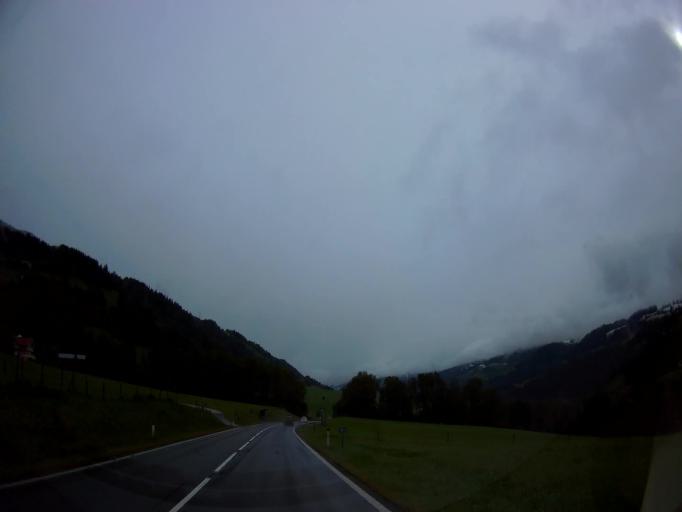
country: AT
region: Styria
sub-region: Politischer Bezirk Liezen
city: Aich
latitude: 47.4240
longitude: 13.8386
